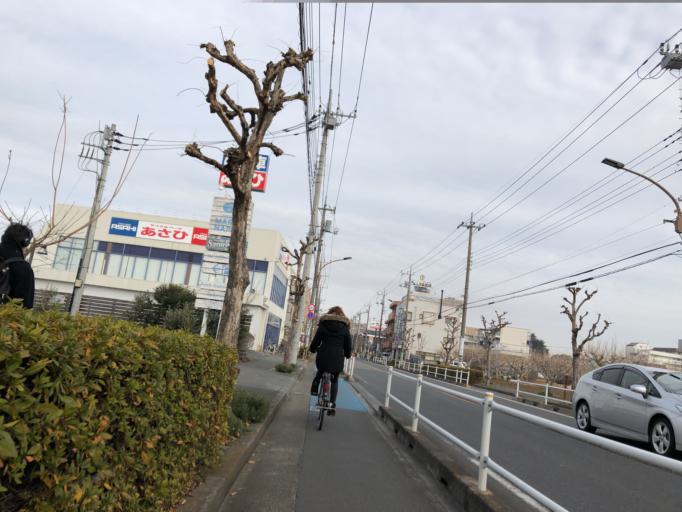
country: JP
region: Tokyo
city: Kamirenjaku
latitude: 35.6930
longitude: 139.5457
